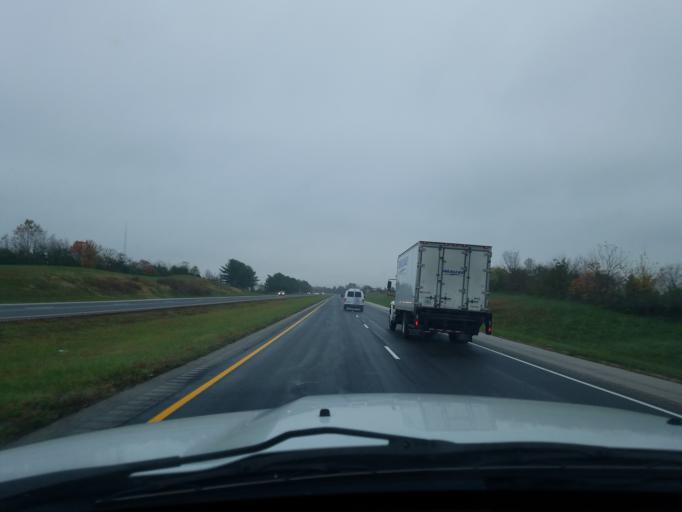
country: US
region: Kentucky
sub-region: Larue County
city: Hodgenville
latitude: 37.5582
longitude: -85.7448
